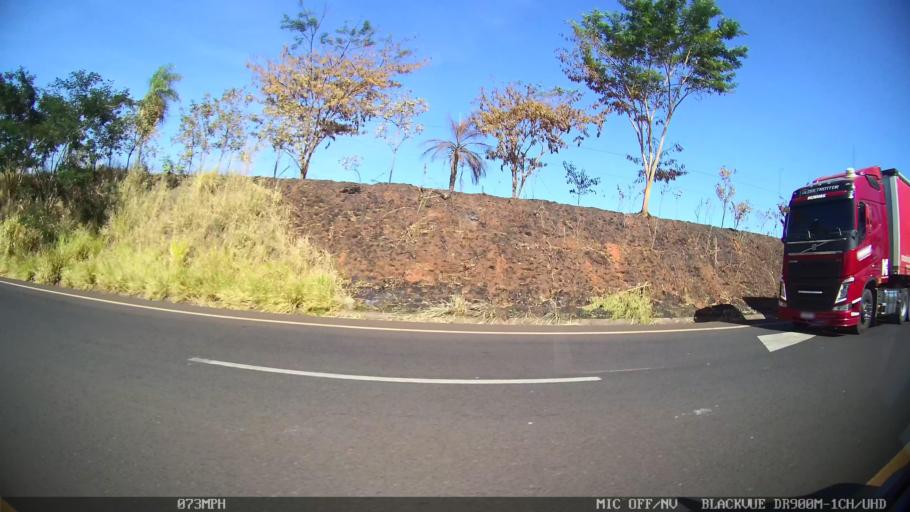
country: BR
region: Sao Paulo
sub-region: Barretos
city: Barretos
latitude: -20.5992
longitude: -48.7238
